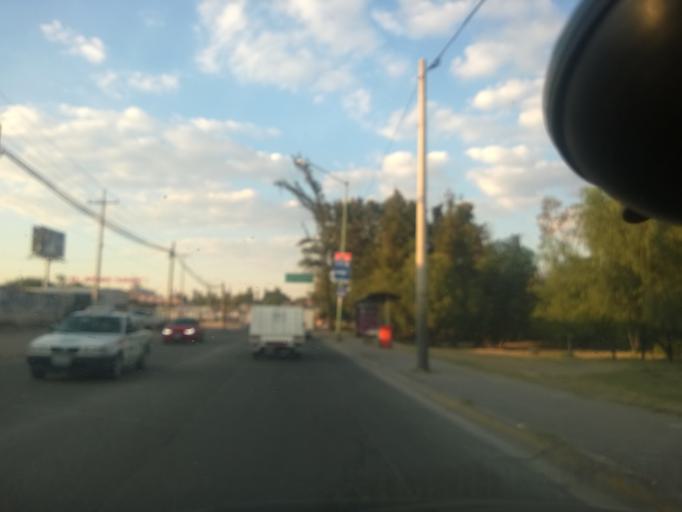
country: MX
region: Guanajuato
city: Leon
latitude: 21.1681
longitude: -101.6857
